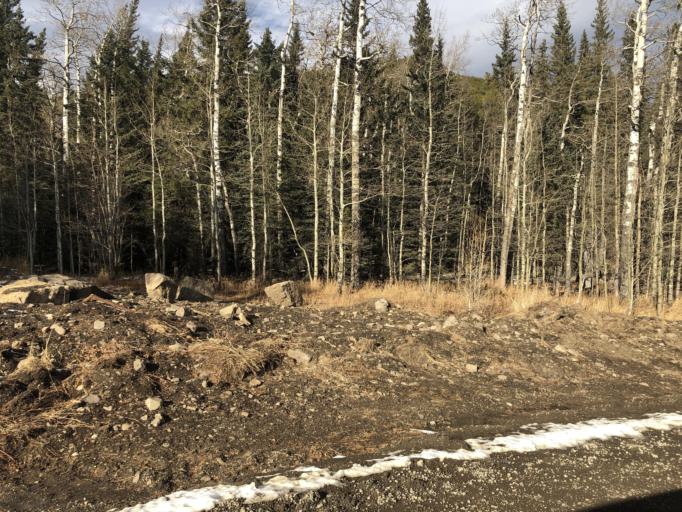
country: CA
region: Alberta
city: Canmore
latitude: 51.0106
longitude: -114.9230
